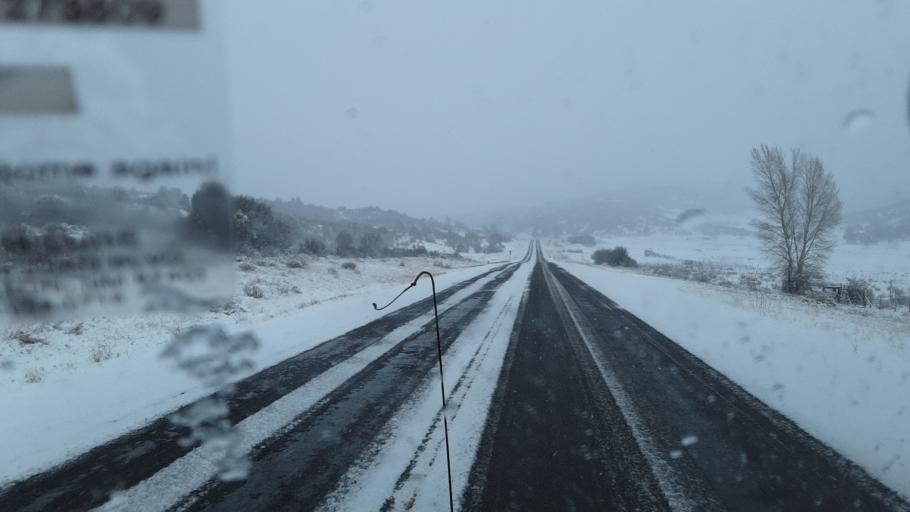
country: US
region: New Mexico
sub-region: Rio Arriba County
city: Chama
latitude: 36.9601
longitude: -106.7852
